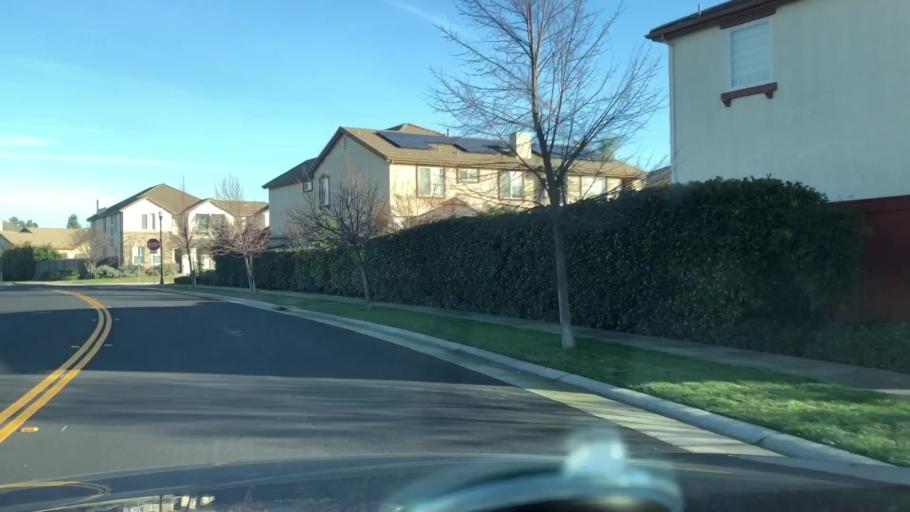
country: US
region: California
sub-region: Sacramento County
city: Laguna
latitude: 38.3985
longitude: -121.4070
